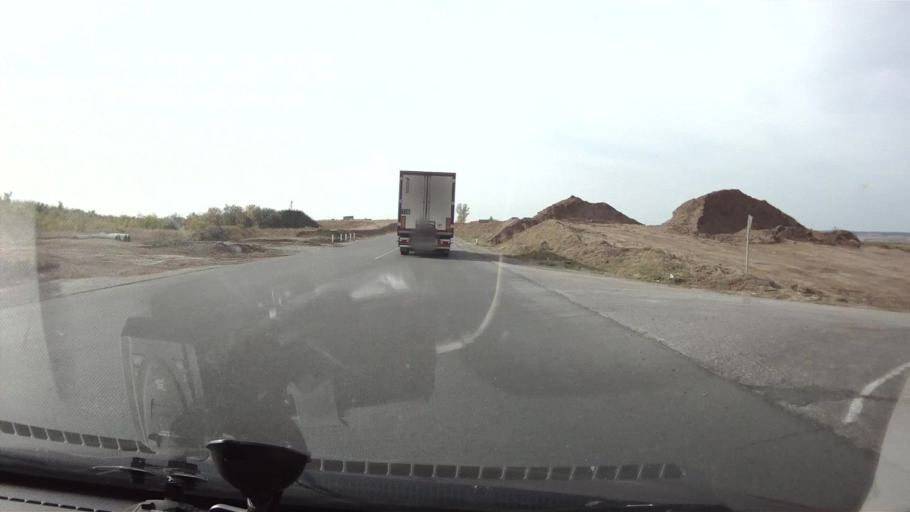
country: RU
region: Saratov
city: Sennoy
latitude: 52.1597
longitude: 47.0612
